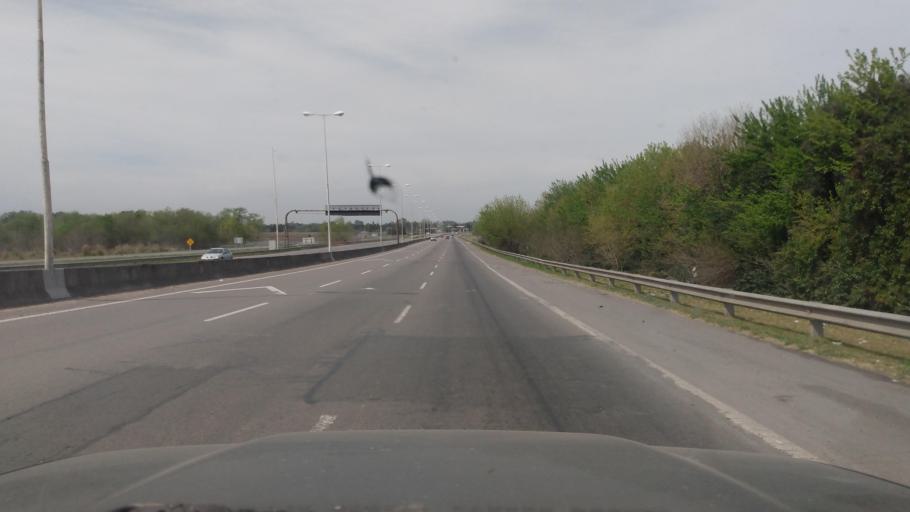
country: AR
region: Buenos Aires
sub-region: Partido de Pilar
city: Pilar
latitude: -34.4056
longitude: -59.0111
